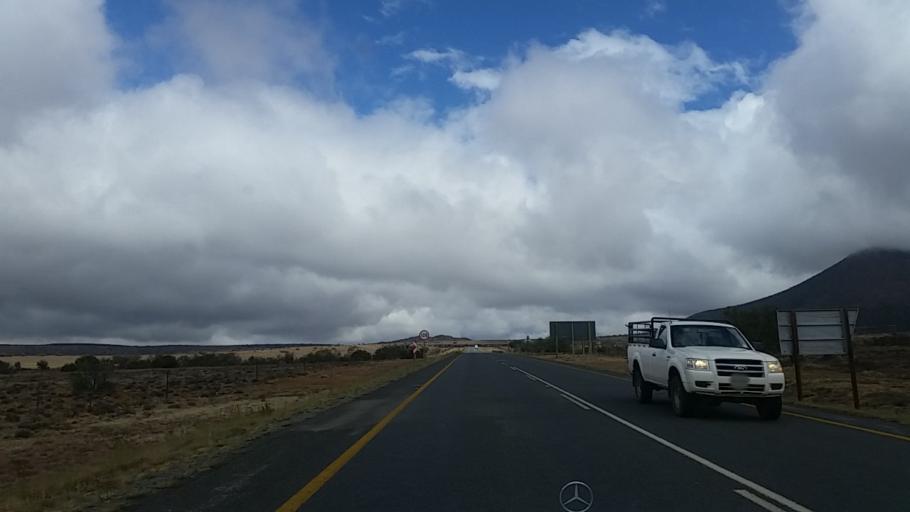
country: ZA
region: Eastern Cape
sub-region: Cacadu District Municipality
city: Graaff-Reinet
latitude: -32.0326
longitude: 24.6251
